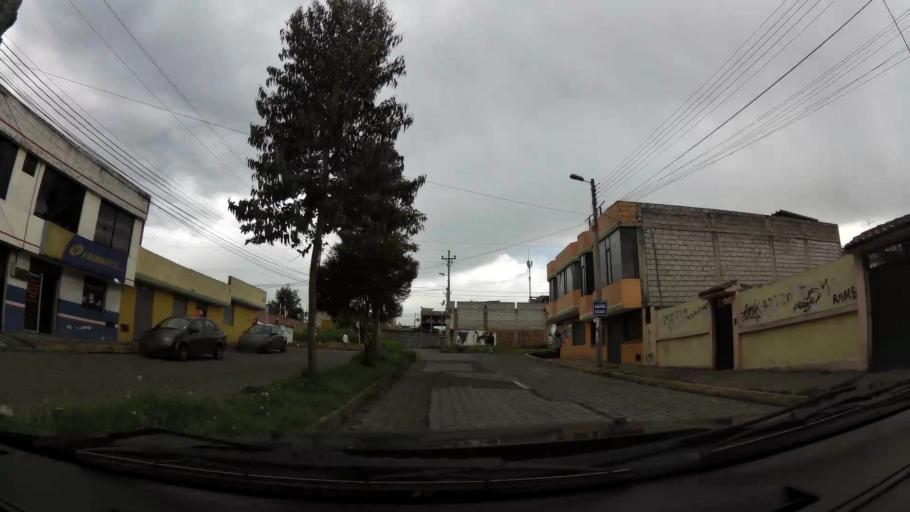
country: EC
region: Pichincha
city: Quito
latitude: -0.3093
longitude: -78.5538
